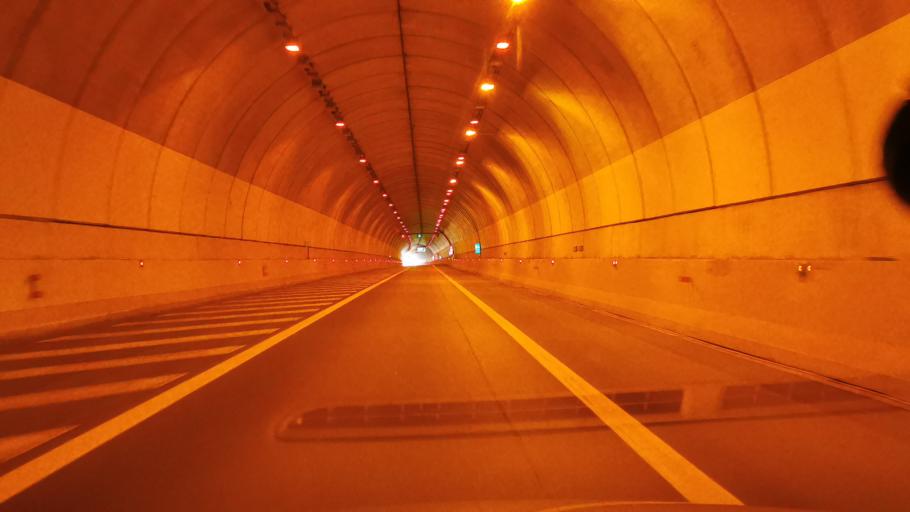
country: IT
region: Piedmont
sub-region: Provincia di Cuneo
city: Cuneo
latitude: 44.4265
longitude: 7.5683
